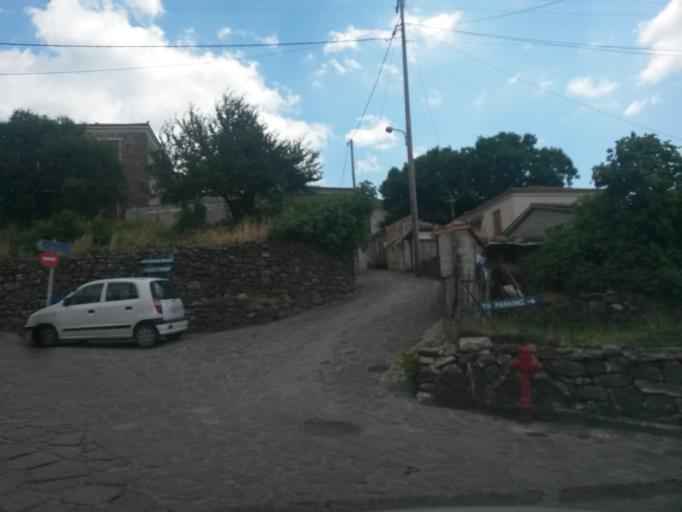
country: GR
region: North Aegean
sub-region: Nomos Lesvou
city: Eresos
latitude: 39.2259
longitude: 26.0496
